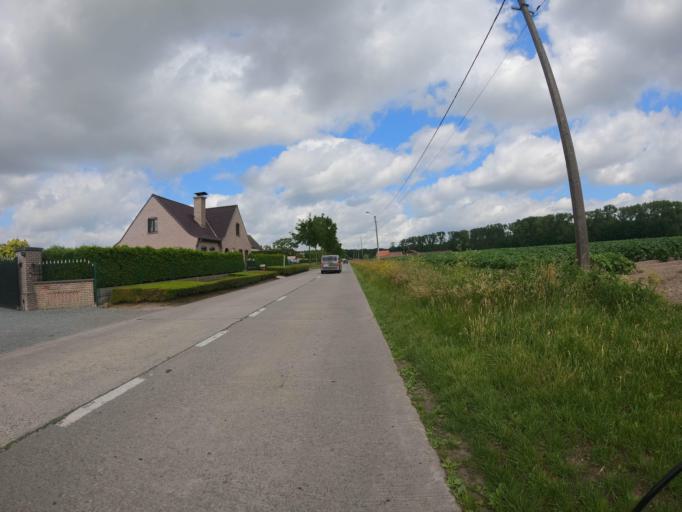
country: BE
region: Flanders
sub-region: Provincie West-Vlaanderen
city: Ruiselede
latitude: 51.0652
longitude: 3.3714
